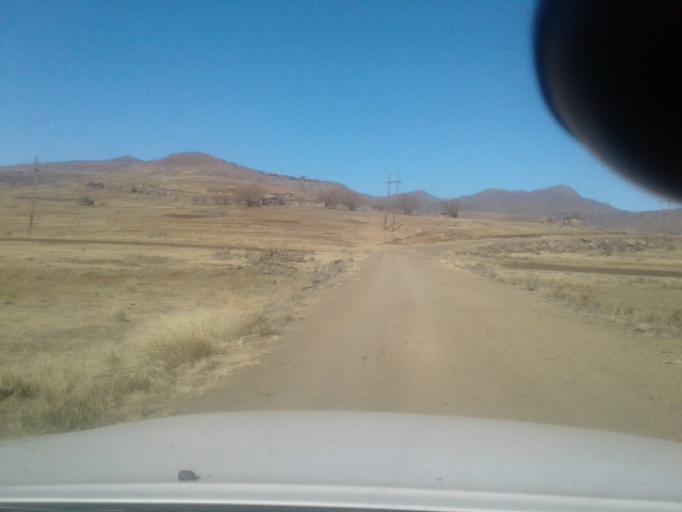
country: LS
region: Maseru
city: Nako
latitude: -29.3732
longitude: 28.0210
